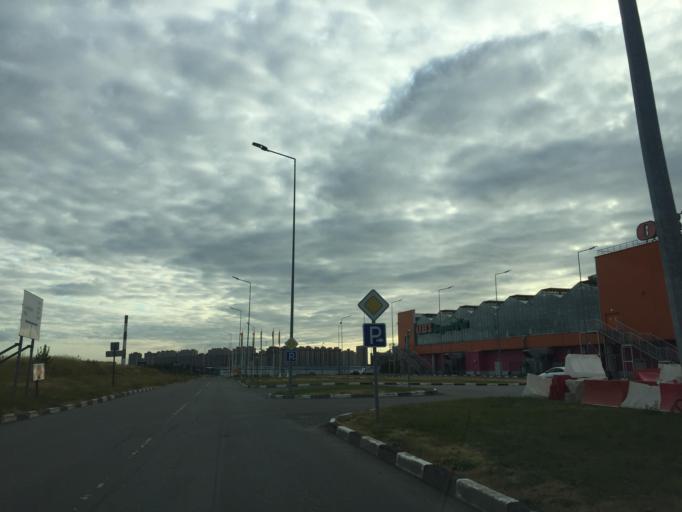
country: RU
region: Leningrad
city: Bugry
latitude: 60.0893
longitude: 30.3835
